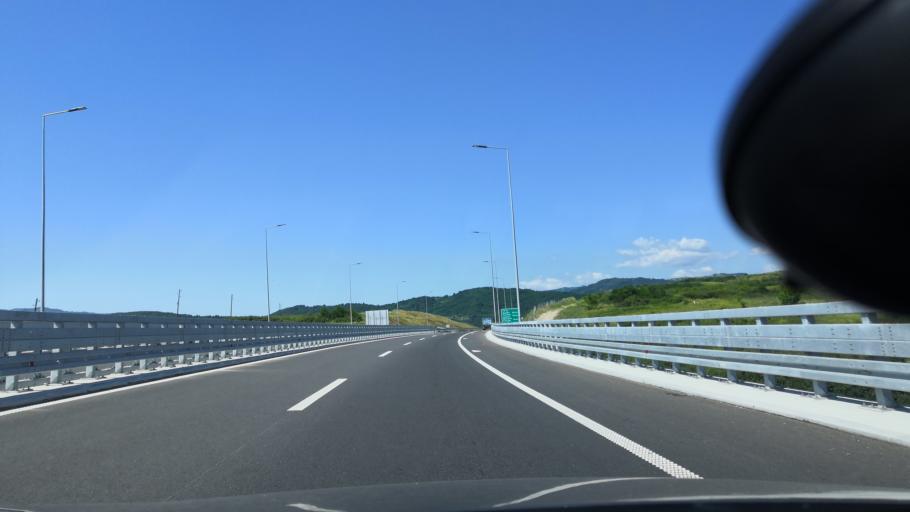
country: RS
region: Central Serbia
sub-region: Pcinjski Okrug
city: Vladicin Han
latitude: 42.7116
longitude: 22.0727
